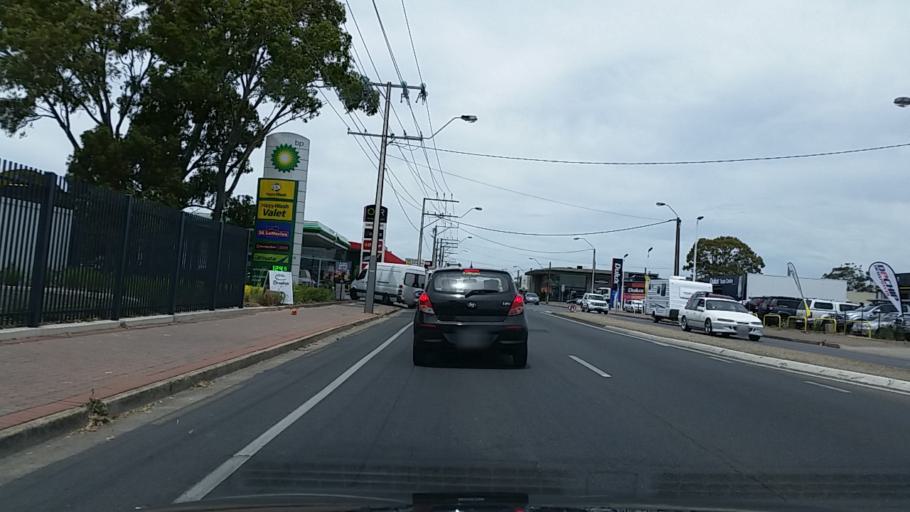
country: AU
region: South Australia
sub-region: Marion
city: Clovelly Park
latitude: -34.9970
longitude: 138.5752
